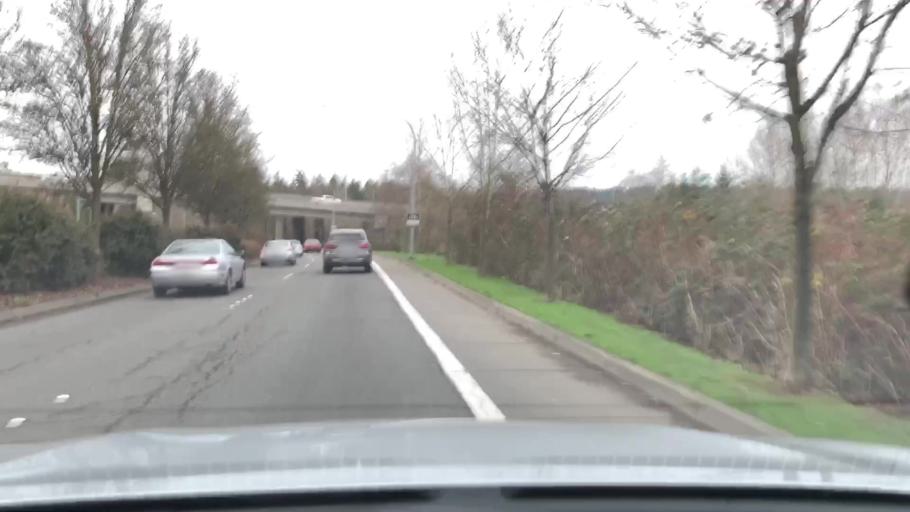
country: US
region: Washington
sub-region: King County
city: Redmond
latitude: 47.6657
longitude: -122.1268
